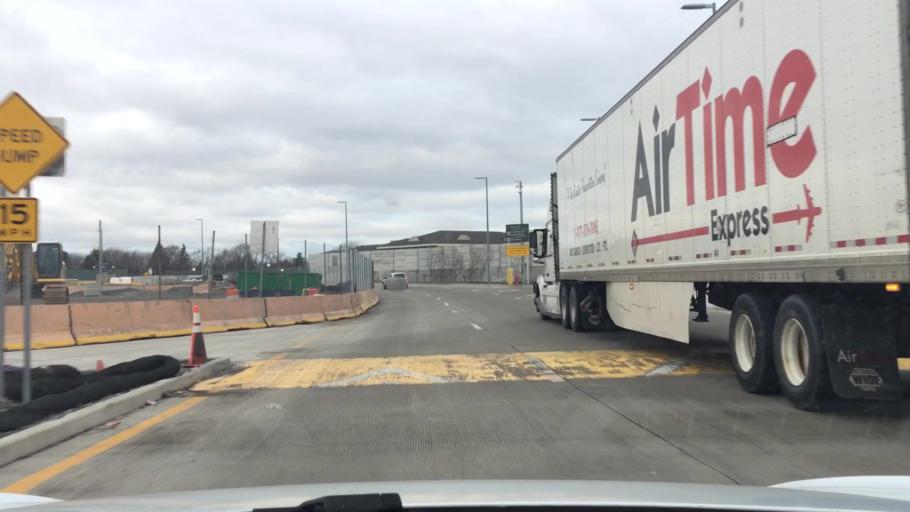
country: US
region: New York
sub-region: Niagara County
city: Lewiston
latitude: 43.1523
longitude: -79.0337
